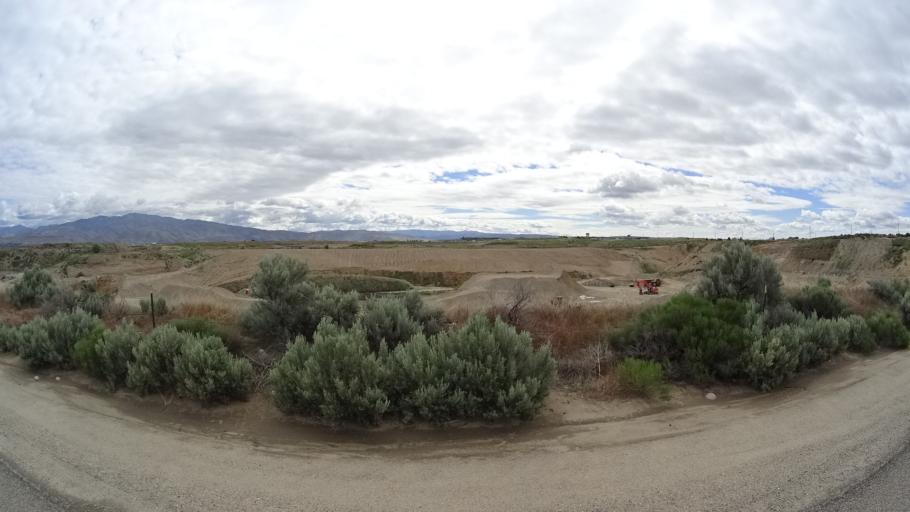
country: US
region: Idaho
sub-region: Ada County
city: Boise
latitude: 43.5513
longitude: -116.1877
